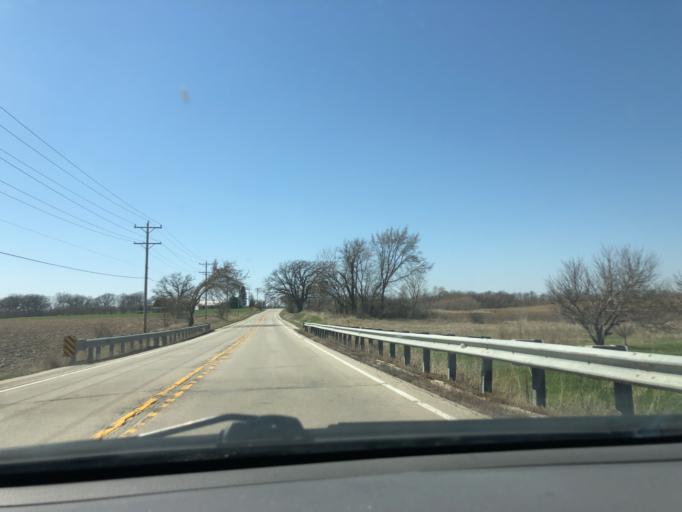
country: US
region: Illinois
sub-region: Kane County
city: Hampshire
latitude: 42.1310
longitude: -88.4925
